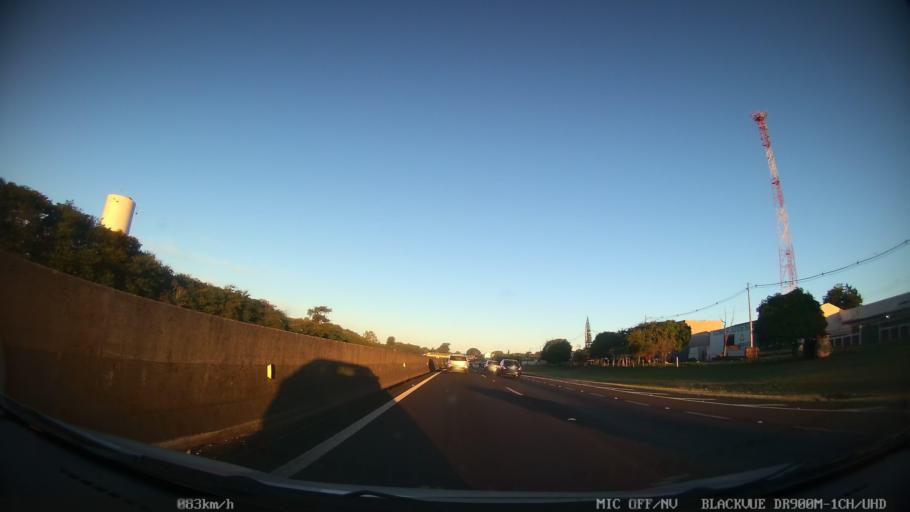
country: BR
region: Sao Paulo
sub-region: Sao Carlos
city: Sao Carlos
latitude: -21.9942
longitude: -47.8792
